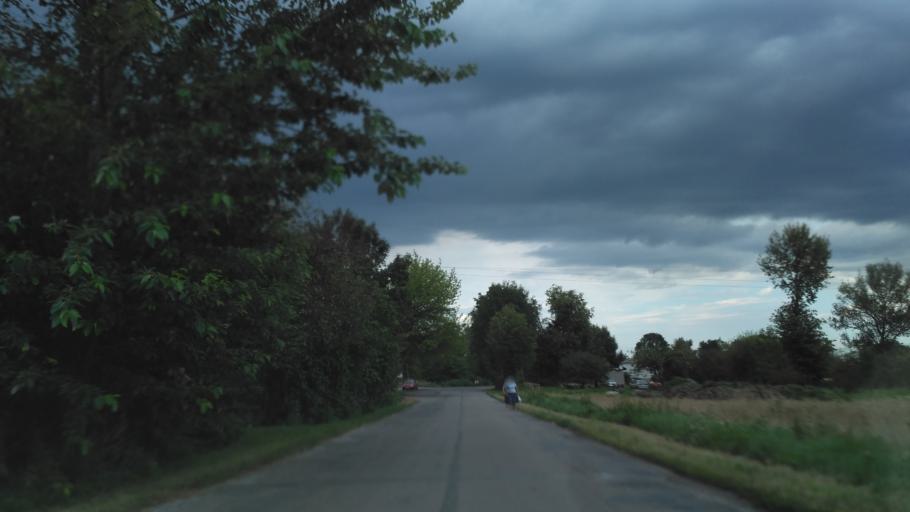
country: PL
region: Lublin Voivodeship
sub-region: Powiat leczynski
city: Milejow
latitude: 51.2121
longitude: 22.8864
